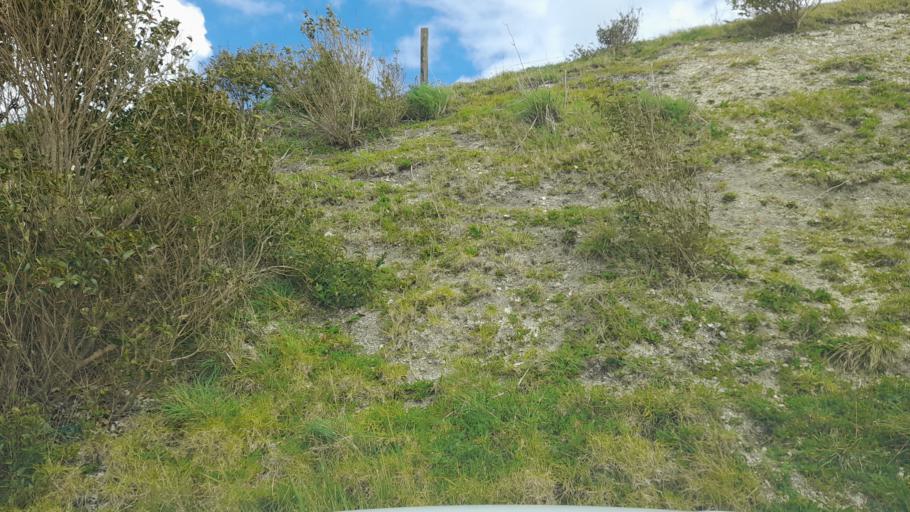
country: NZ
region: Auckland
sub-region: Auckland
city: Wellsford
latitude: -36.2233
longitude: 174.3214
